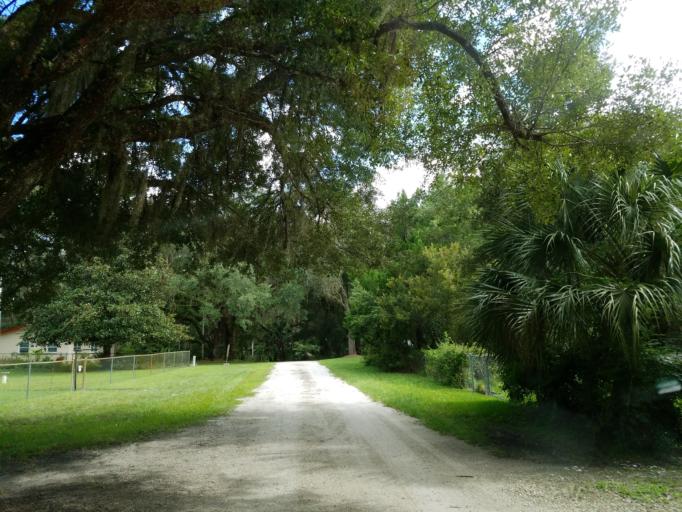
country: US
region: Florida
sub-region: Alachua County
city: Gainesville
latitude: 29.5040
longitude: -82.2741
